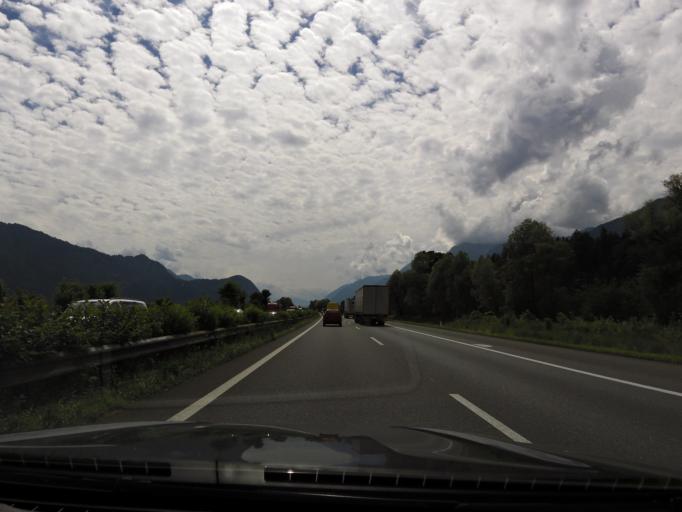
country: AT
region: Tyrol
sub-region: Politischer Bezirk Kufstein
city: Breitenbach am Inn
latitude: 47.4656
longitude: 11.9475
